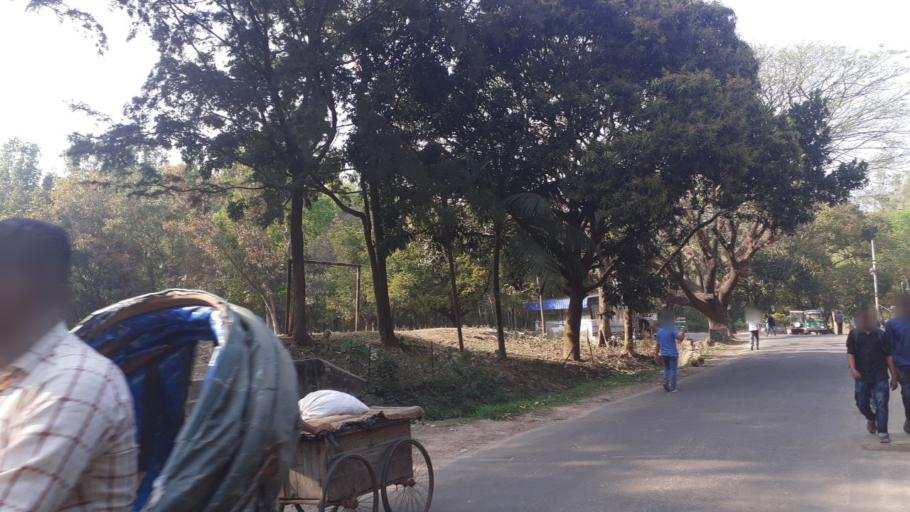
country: BD
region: Chittagong
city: Raojan
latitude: 22.4738
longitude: 91.7933
